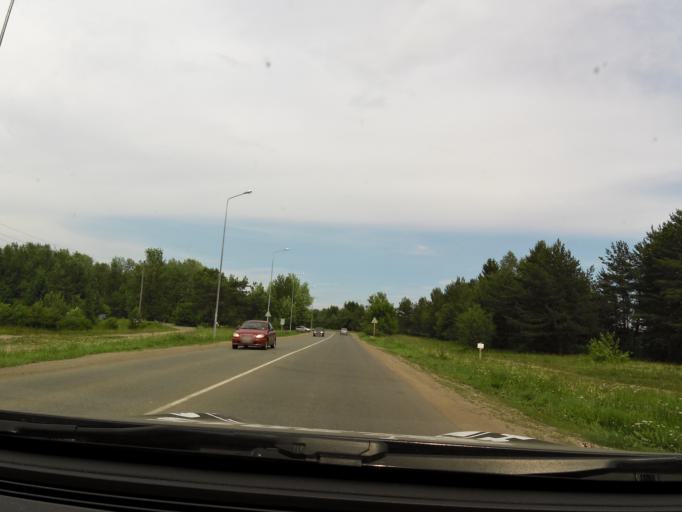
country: RU
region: Kirov
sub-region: Kirovo-Chepetskiy Rayon
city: Kirov
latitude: 58.6181
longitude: 49.7717
